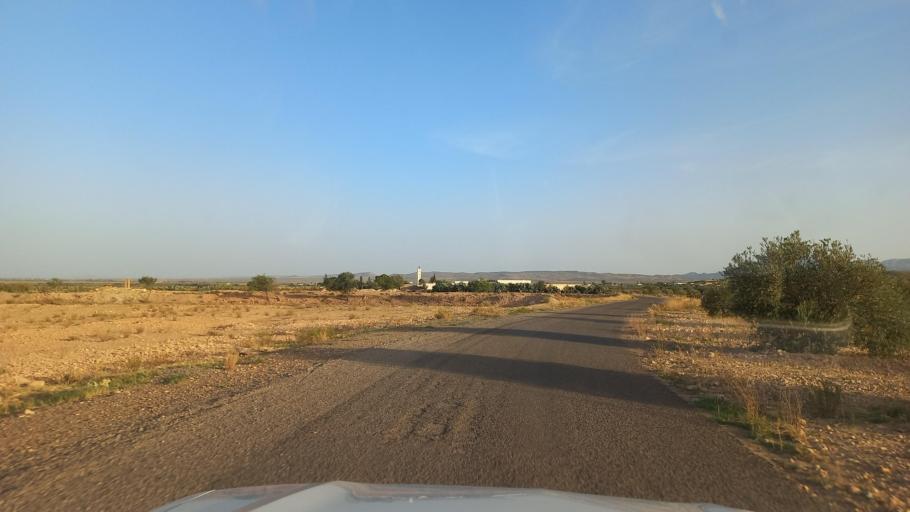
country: TN
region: Al Qasrayn
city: Kasserine
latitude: 35.2686
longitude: 8.9315
